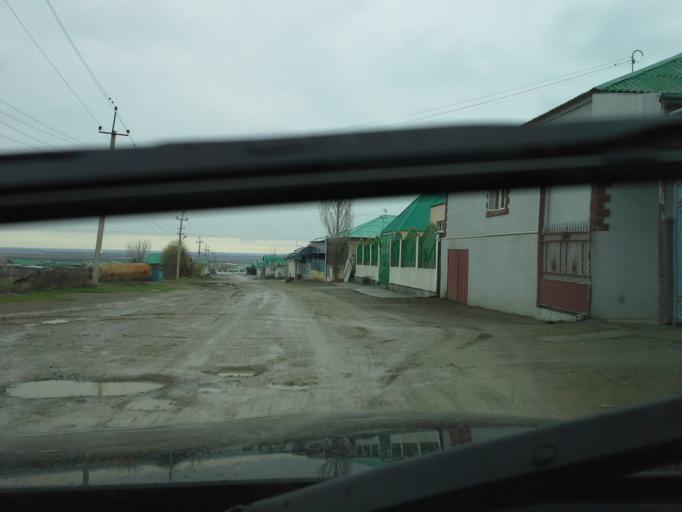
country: TM
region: Ahal
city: Abadan
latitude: 37.9575
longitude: 58.2009
